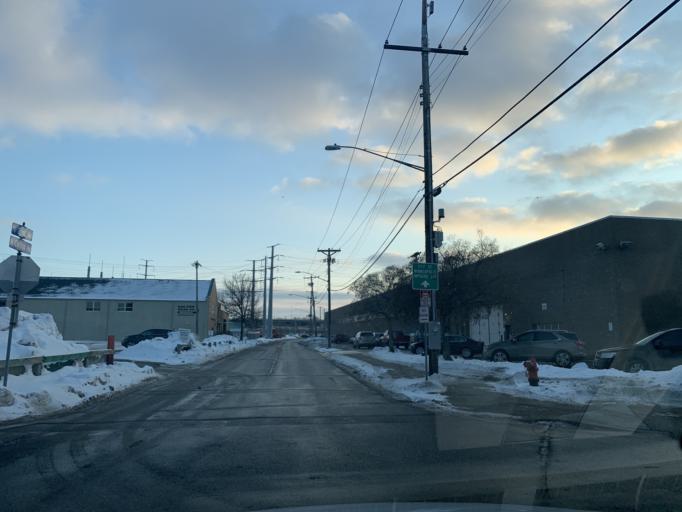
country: US
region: Minnesota
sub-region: Hennepin County
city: Minneapolis
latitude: 44.9790
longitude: -93.2915
